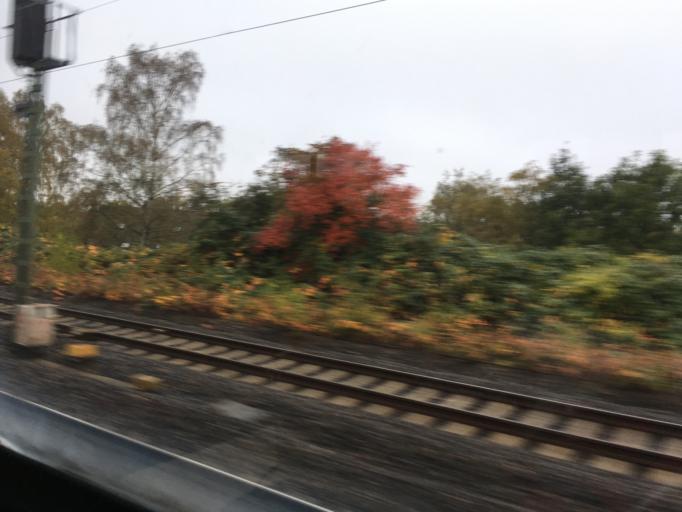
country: DE
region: North Rhine-Westphalia
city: Bochum-Hordel
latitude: 51.5090
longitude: 7.2032
